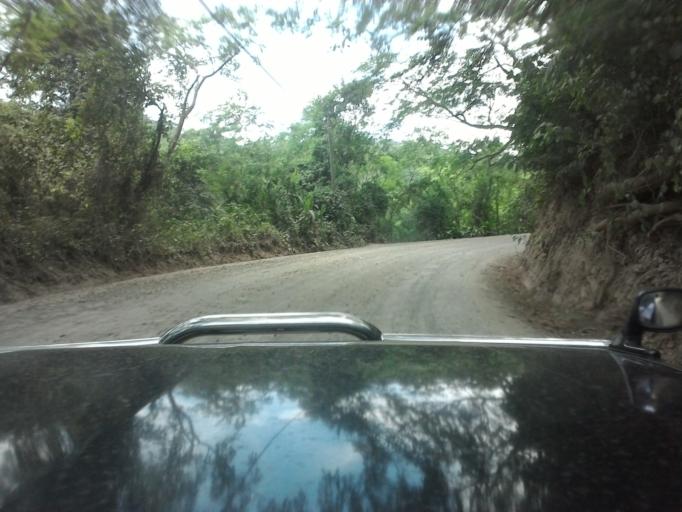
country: CR
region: Guanacaste
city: Juntas
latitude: 10.2199
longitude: -84.8539
